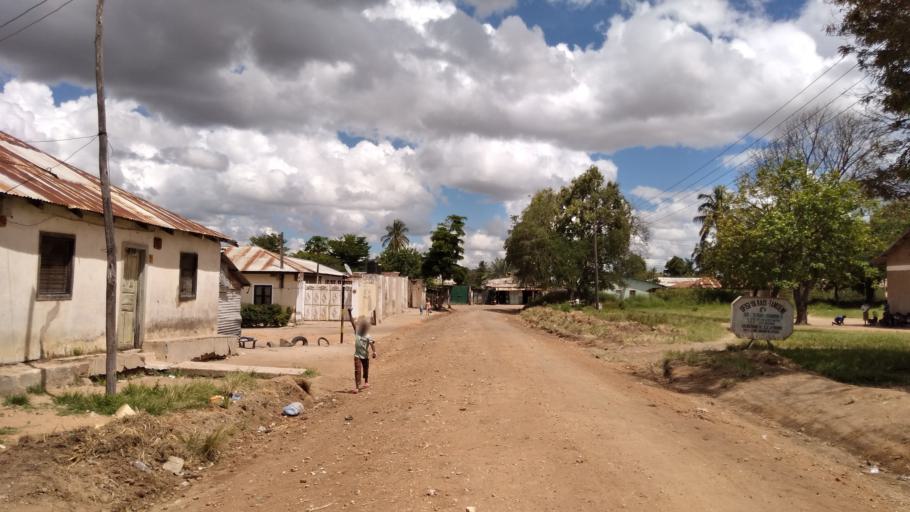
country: TZ
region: Dodoma
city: Dodoma
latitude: -6.1650
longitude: 35.7385
